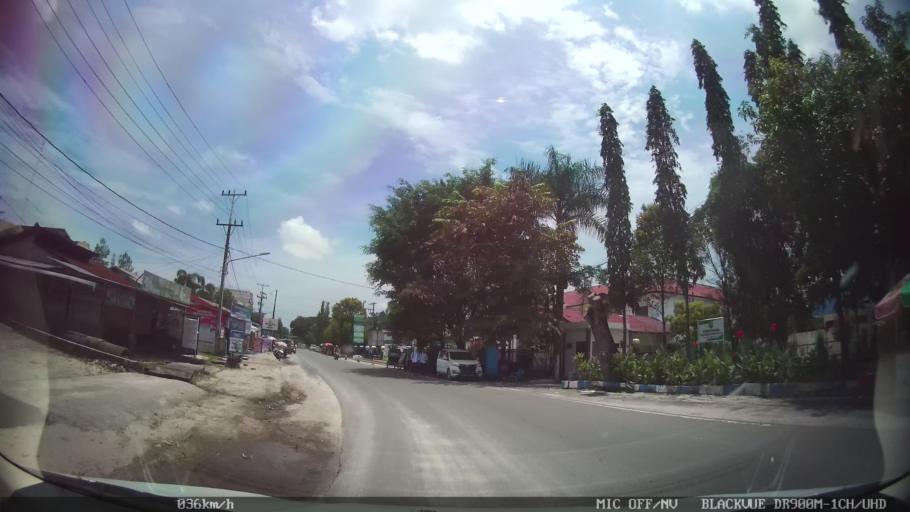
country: ID
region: North Sumatra
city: Percut
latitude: 3.5576
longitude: 98.8651
